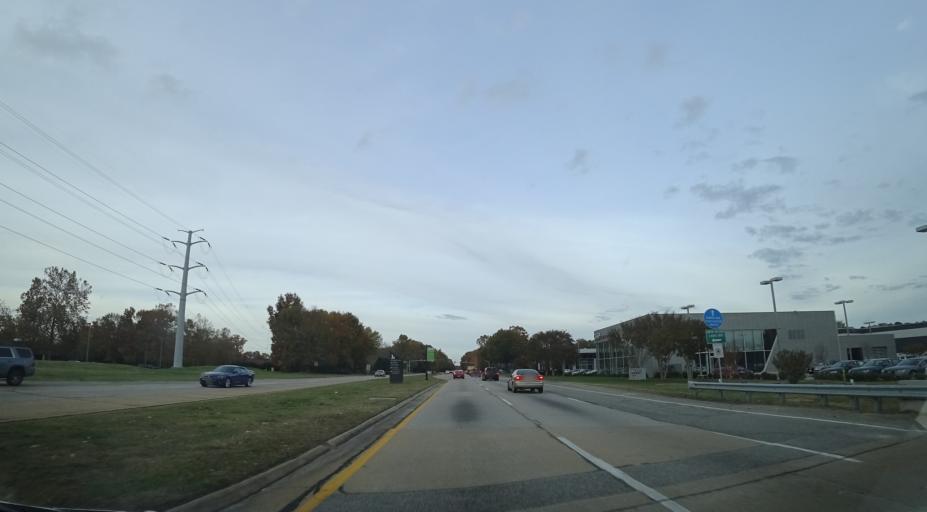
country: US
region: Virginia
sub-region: City of Hampton
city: Hampton
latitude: 37.0613
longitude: -76.4008
